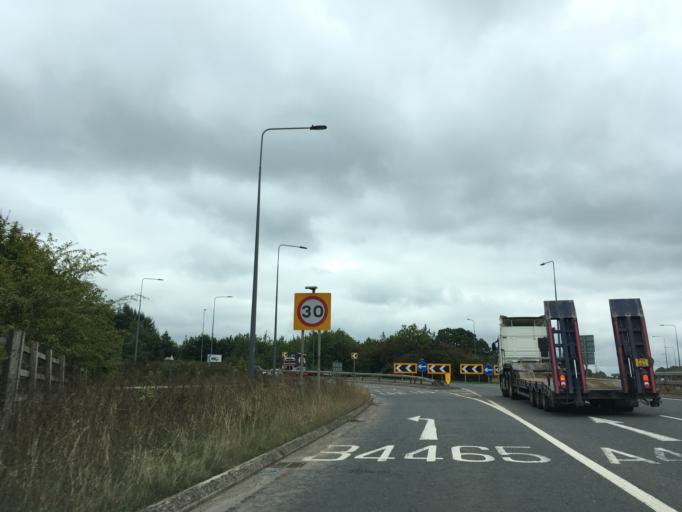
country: GB
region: England
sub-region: South Gloucestershire
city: Siston
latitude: 51.4876
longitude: -2.4695
